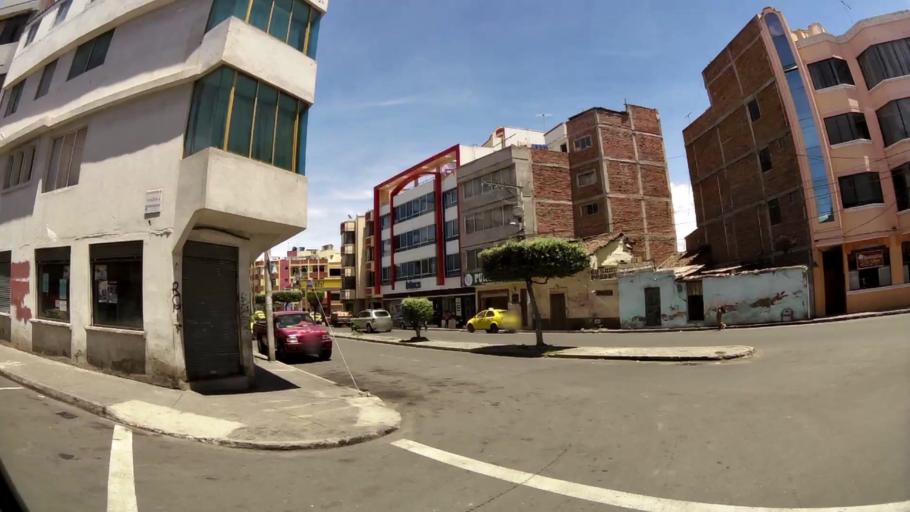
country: EC
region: Chimborazo
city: Riobamba
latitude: -1.6662
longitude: -78.6495
